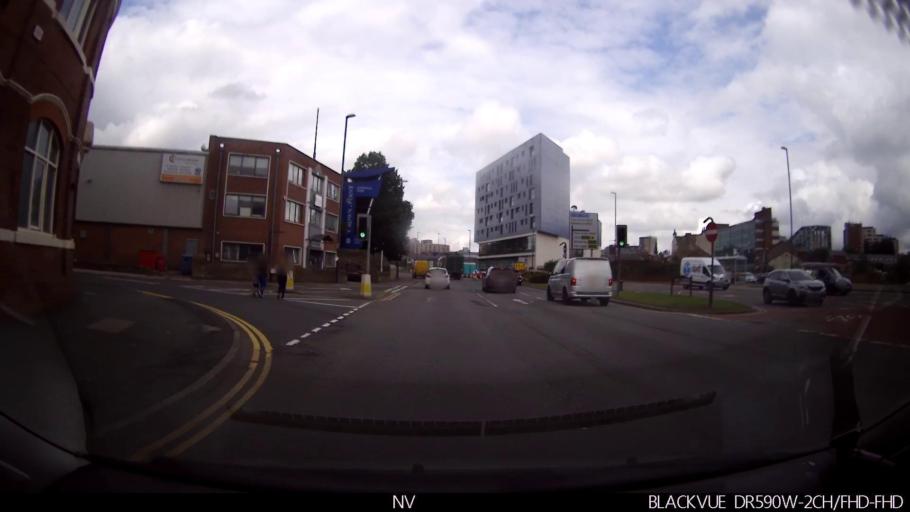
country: GB
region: England
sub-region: City and Borough of Leeds
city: Leeds
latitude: 53.7899
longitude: -1.5382
